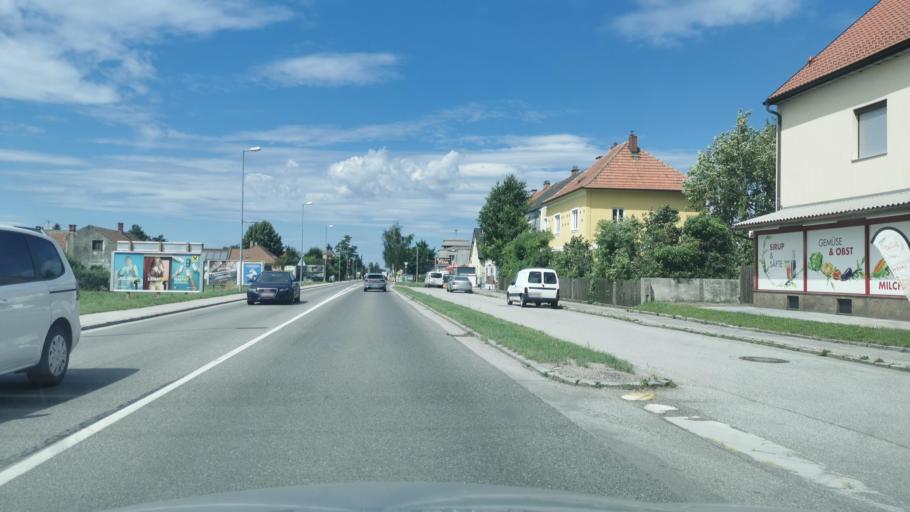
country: AT
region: Lower Austria
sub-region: Politischer Bezirk Sankt Polten
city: Wilhelmsburg
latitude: 48.1412
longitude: 15.6134
